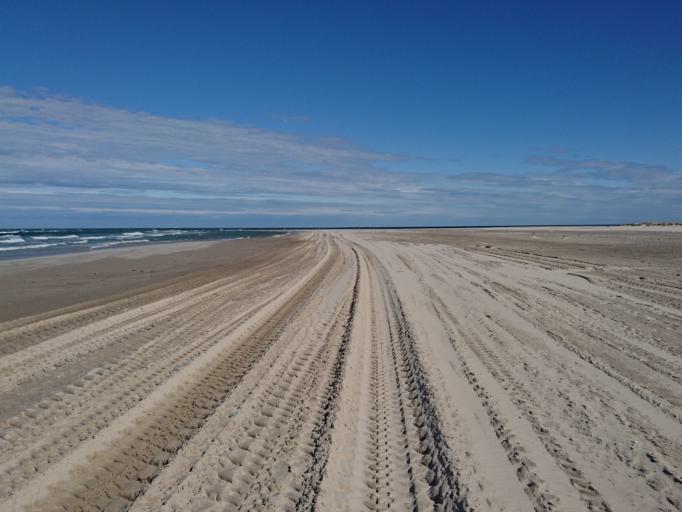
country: DK
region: North Denmark
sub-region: Frederikshavn Kommune
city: Skagen
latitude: 57.7476
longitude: 10.6455
